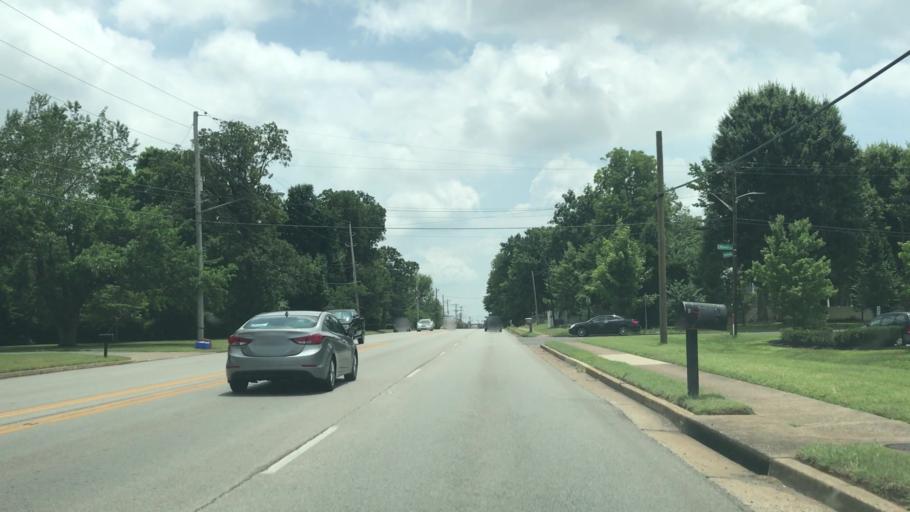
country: US
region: Kentucky
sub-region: Warren County
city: Bowling Green
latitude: 36.9748
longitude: -86.4365
